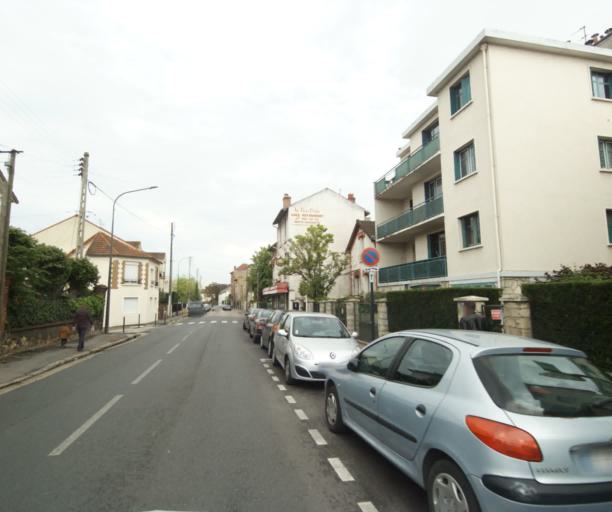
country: FR
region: Ile-de-France
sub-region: Departement du Val-d'Oise
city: Argenteuil
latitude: 48.9506
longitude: 2.2442
